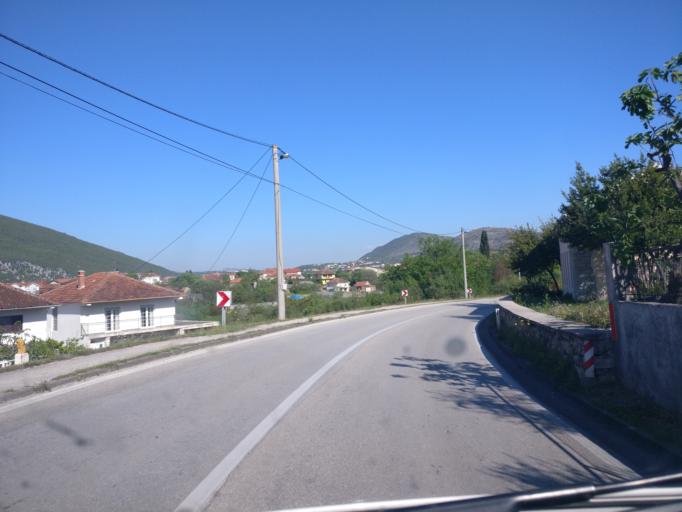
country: BA
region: Federation of Bosnia and Herzegovina
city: Capljina
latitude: 43.1243
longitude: 17.6819
